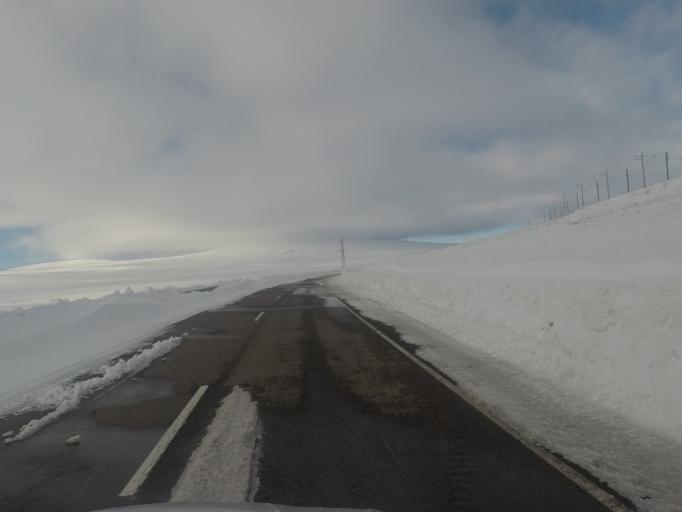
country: GE
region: Kvemo Kartli
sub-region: Tsalka
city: Tsalka
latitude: 41.4777
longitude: 43.8503
